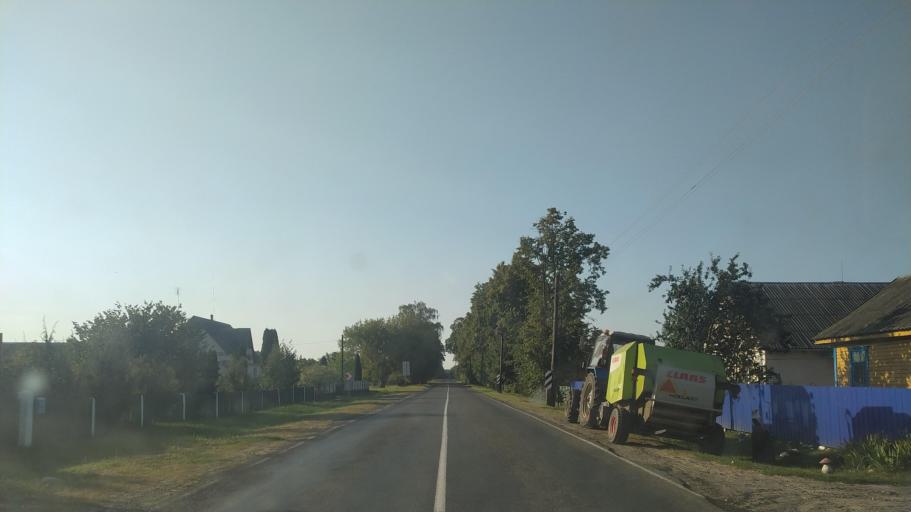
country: BY
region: Brest
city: Drahichyn
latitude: 52.2919
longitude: 25.0661
